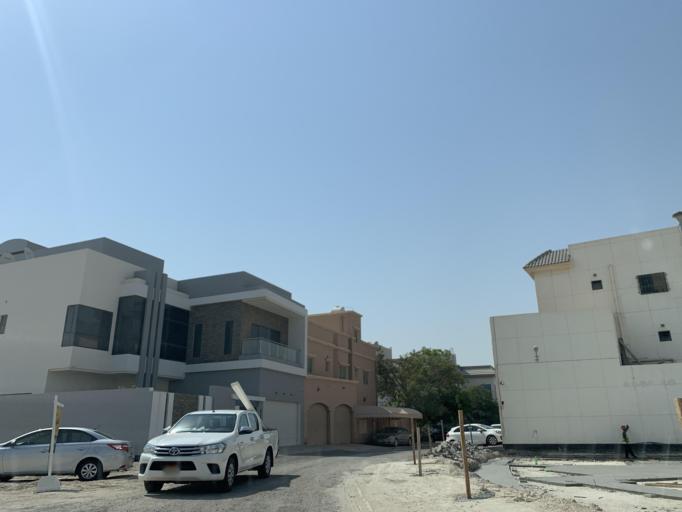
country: BH
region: Manama
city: Jidd Hafs
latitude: 26.1995
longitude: 50.5119
